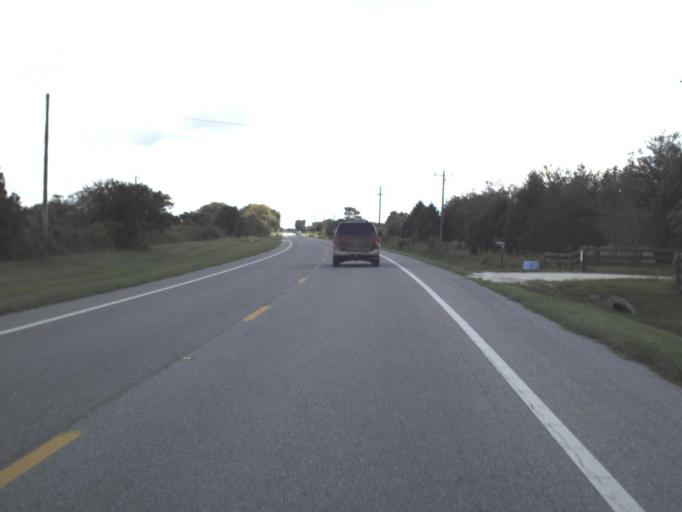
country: US
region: Florida
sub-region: DeSoto County
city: Arcadia
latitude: 27.3113
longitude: -82.1025
